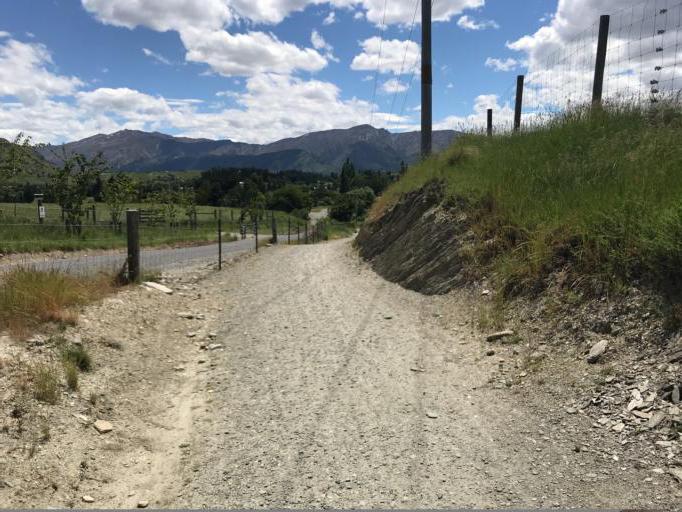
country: NZ
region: Otago
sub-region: Queenstown-Lakes District
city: Arrowtown
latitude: -44.9933
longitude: 168.8555
